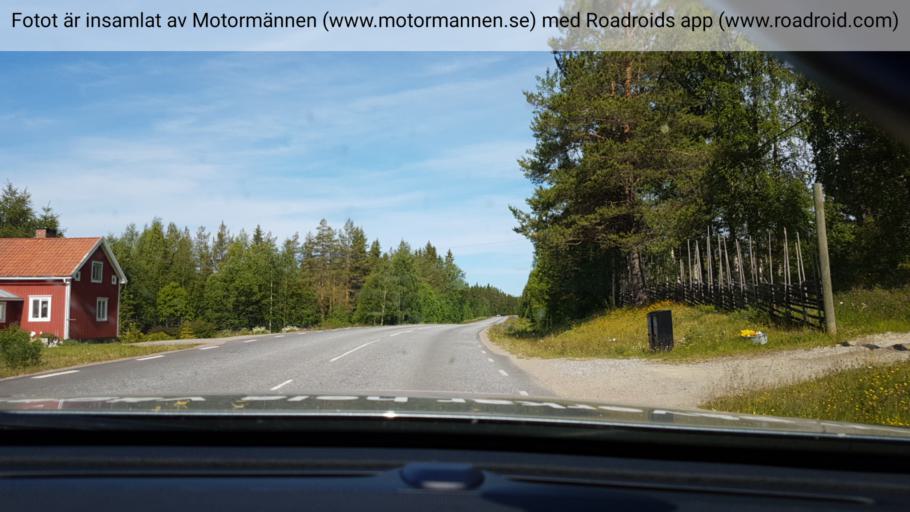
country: SE
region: Vaesterbotten
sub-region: Dorotea Kommun
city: Dorotea
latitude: 64.2648
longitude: 16.3573
